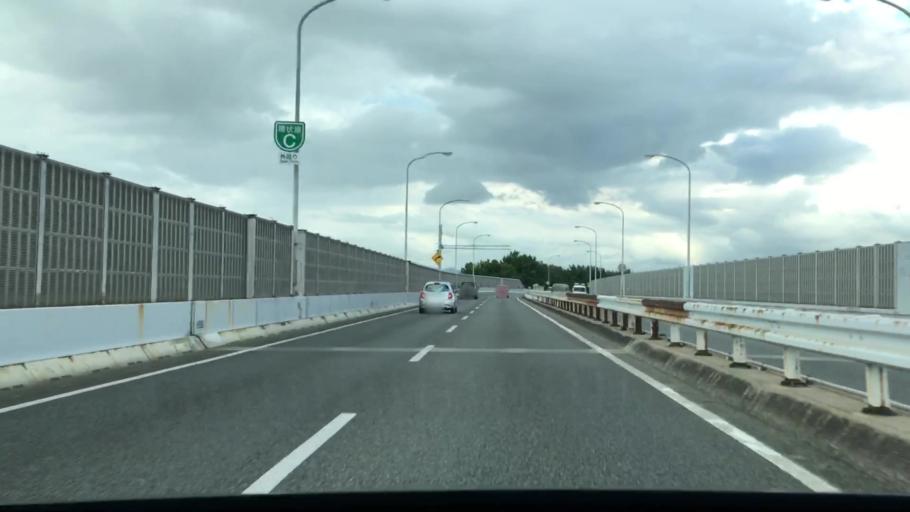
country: JP
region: Fukuoka
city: Fukuoka-shi
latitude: 33.5991
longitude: 130.3651
